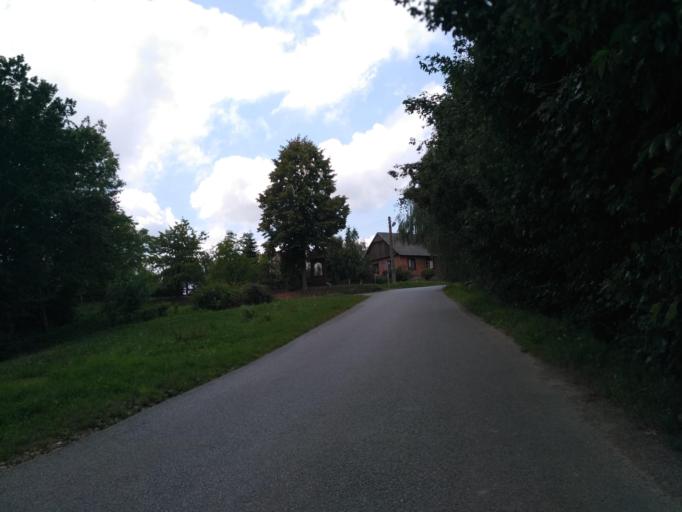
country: PL
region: Subcarpathian Voivodeship
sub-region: Powiat krosnienski
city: Iwonicz-Zdroj
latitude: 49.5843
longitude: 21.7437
